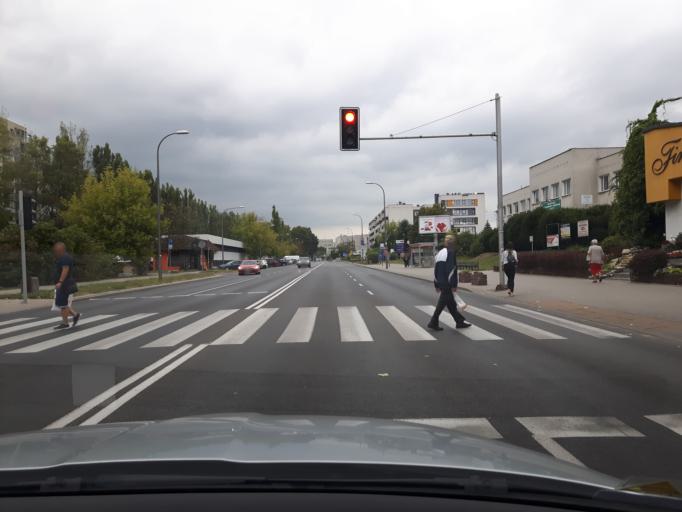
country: PL
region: Masovian Voivodeship
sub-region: Warszawa
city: Ursynow
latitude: 52.1587
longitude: 21.0212
